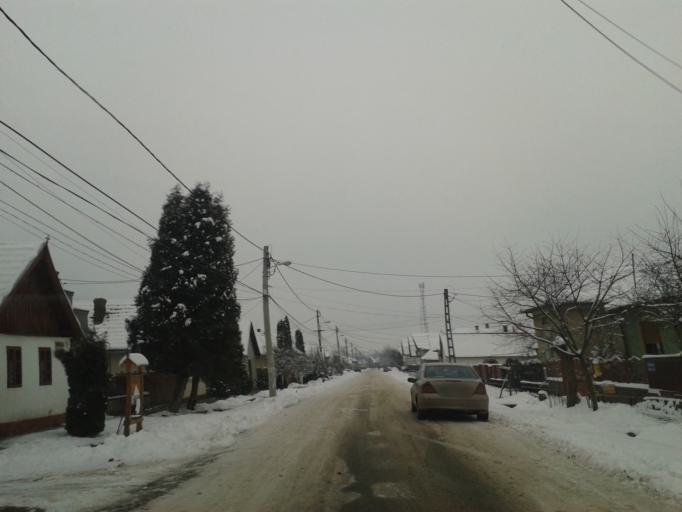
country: RO
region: Hunedoara
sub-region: Municipiul Deva
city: Cristur
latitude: 45.8235
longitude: 22.9364
